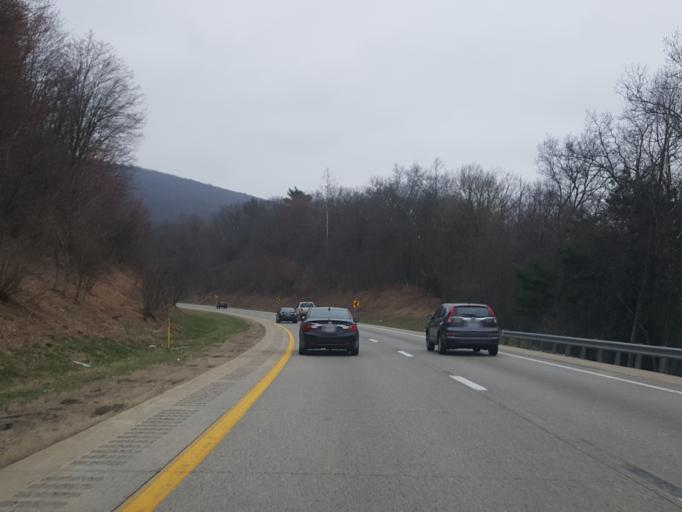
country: US
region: Pennsylvania
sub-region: Lebanon County
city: Jonestown
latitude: 40.4872
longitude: -76.5306
